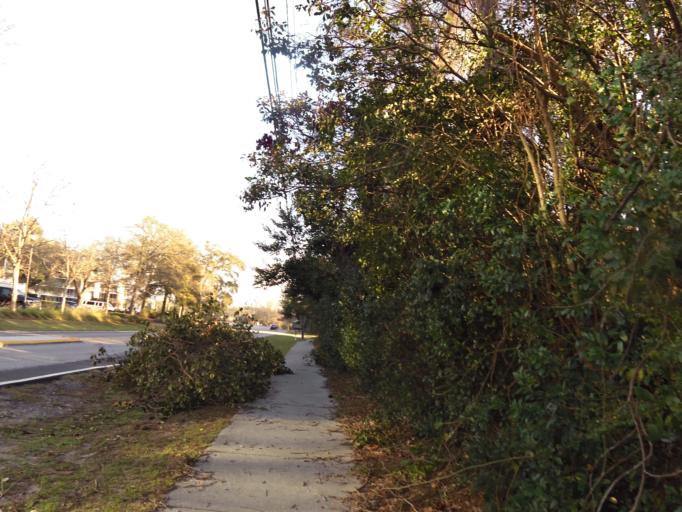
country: US
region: South Carolina
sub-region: Charleston County
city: Mount Pleasant
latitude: 32.8000
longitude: -79.8952
